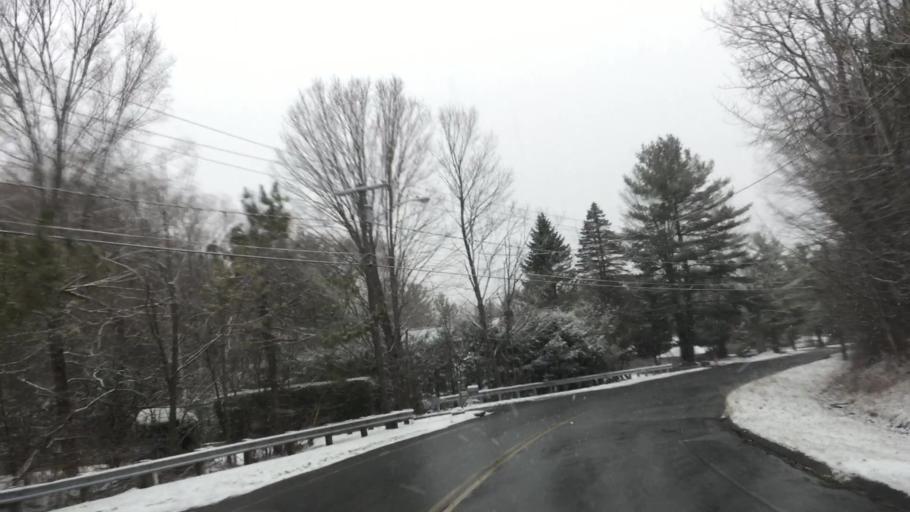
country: US
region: Massachusetts
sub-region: Berkshire County
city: Dalton
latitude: 42.4197
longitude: -73.1910
